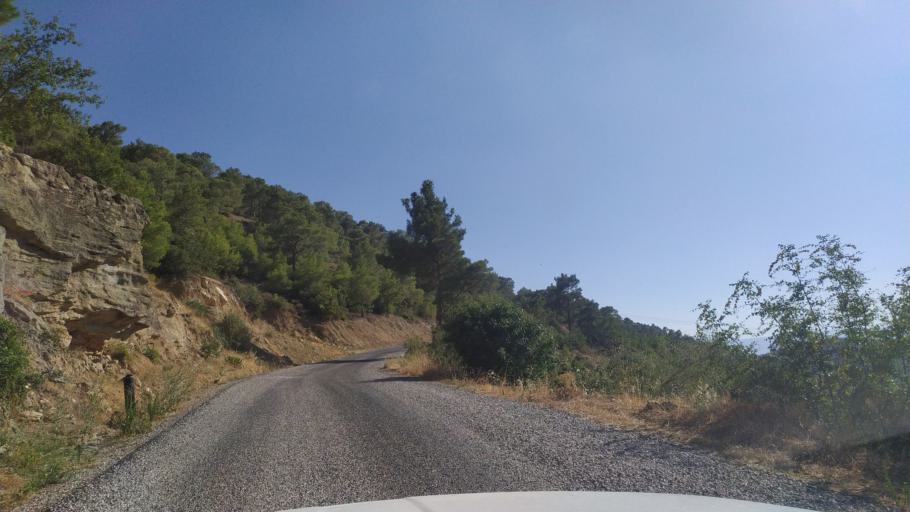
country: TR
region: Mersin
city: Mut
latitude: 36.7046
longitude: 33.4737
